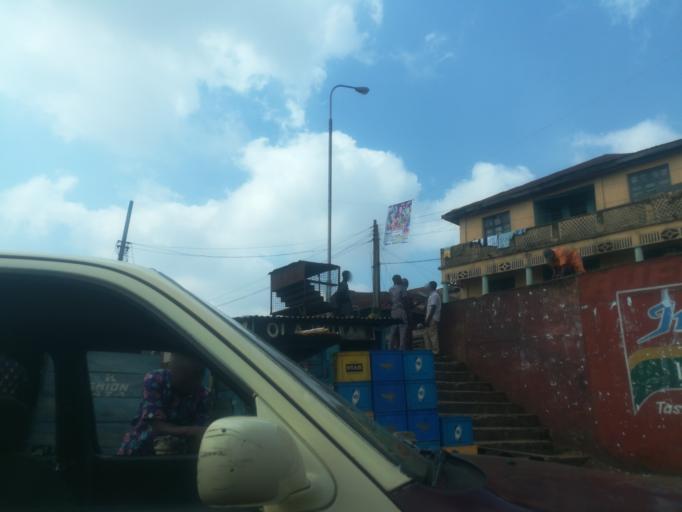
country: NG
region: Oyo
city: Ibadan
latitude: 7.3817
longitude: 3.8994
